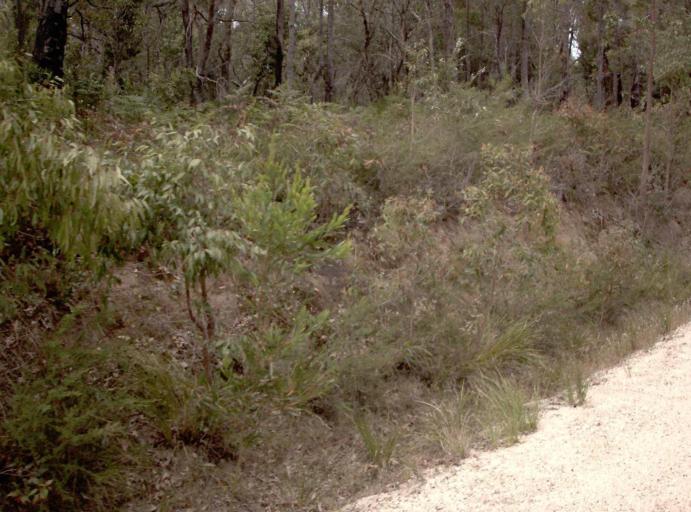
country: AU
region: New South Wales
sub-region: Bega Valley
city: Eden
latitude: -37.4050
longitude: 149.6649
